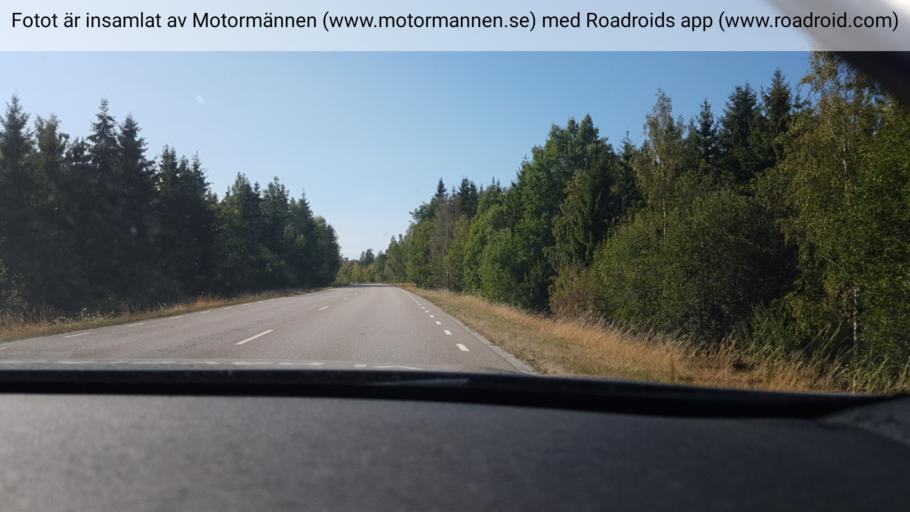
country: SE
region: Vaestra Goetaland
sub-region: Gotene Kommun
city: Goetene
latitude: 58.6234
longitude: 13.4741
